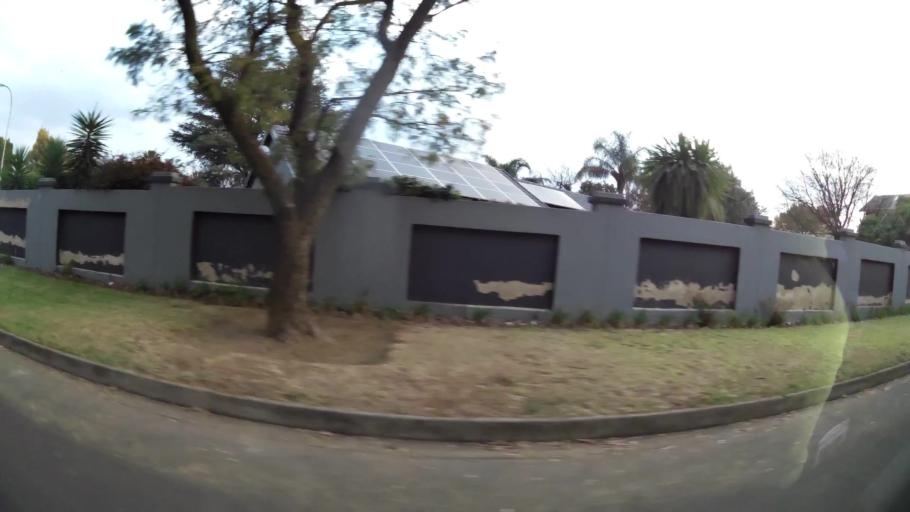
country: ZA
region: Gauteng
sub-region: Ekurhuleni Metropolitan Municipality
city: Benoni
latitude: -26.1743
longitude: 28.3057
